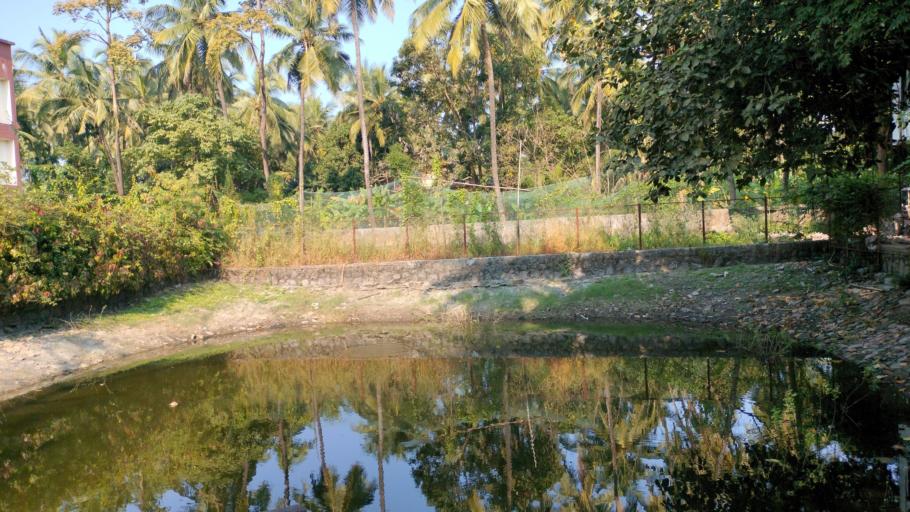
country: IN
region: Maharashtra
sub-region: Thane
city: Bhayandar
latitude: 19.3473
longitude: 72.7987
